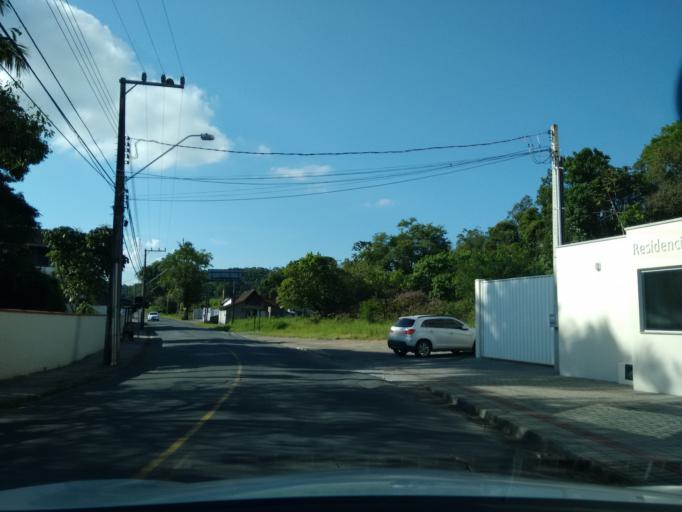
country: BR
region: Santa Catarina
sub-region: Blumenau
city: Blumenau
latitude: -26.8726
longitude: -49.0707
